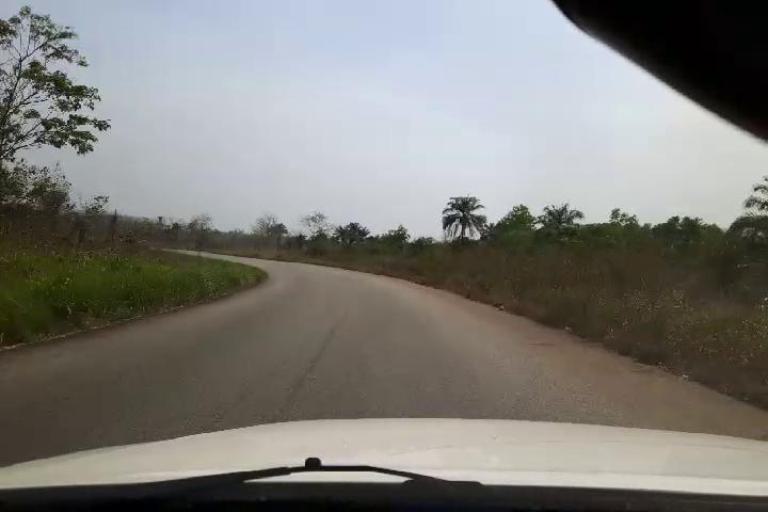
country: SL
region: Northern Province
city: Yonibana
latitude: 8.3962
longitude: -12.1939
